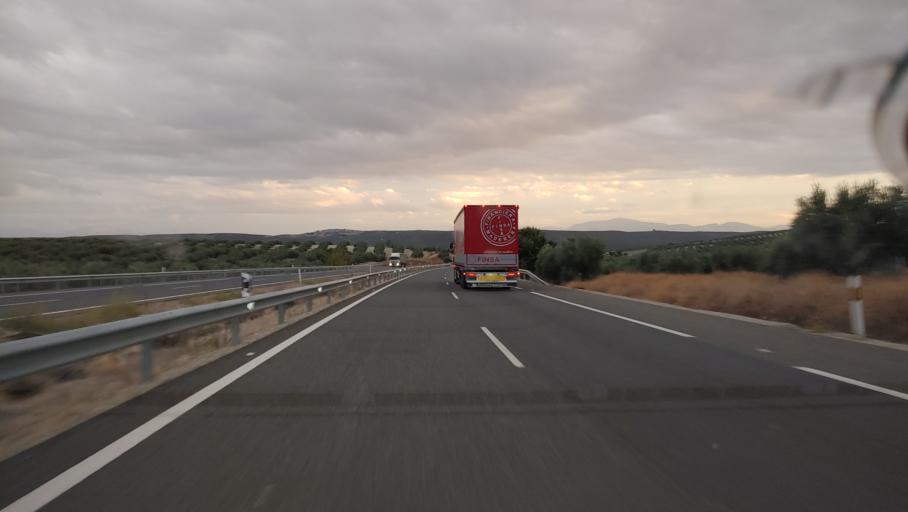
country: ES
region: Andalusia
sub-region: Provincia de Jaen
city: Bailen
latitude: 38.0804
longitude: -3.7360
